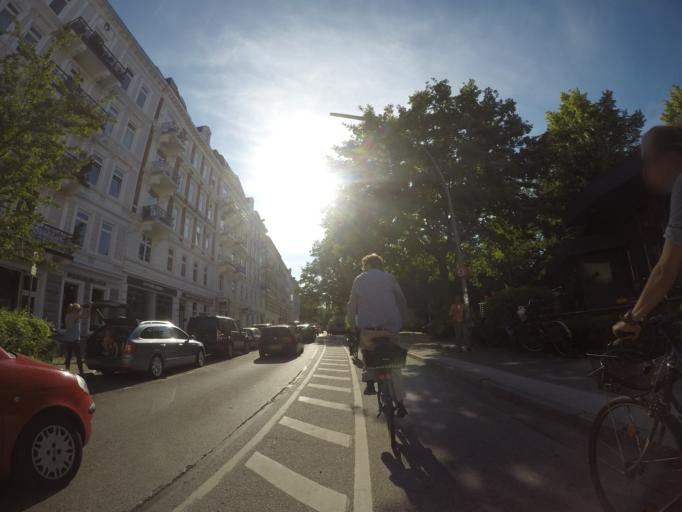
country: DE
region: Hamburg
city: Altona
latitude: 53.5509
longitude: 9.9254
